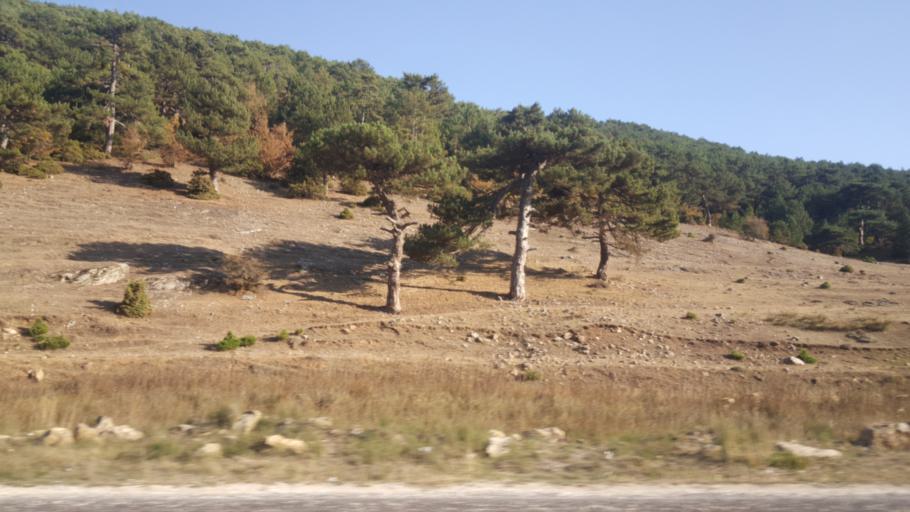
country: TR
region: Afyonkarahisar
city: Ihsaniye
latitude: 39.1023
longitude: 30.5800
